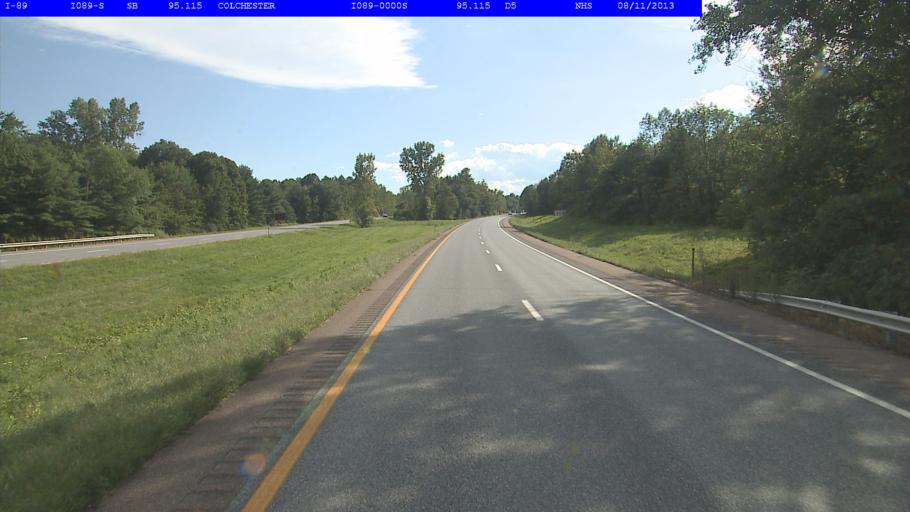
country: US
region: Vermont
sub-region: Chittenden County
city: Colchester
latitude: 44.5520
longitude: -73.1865
